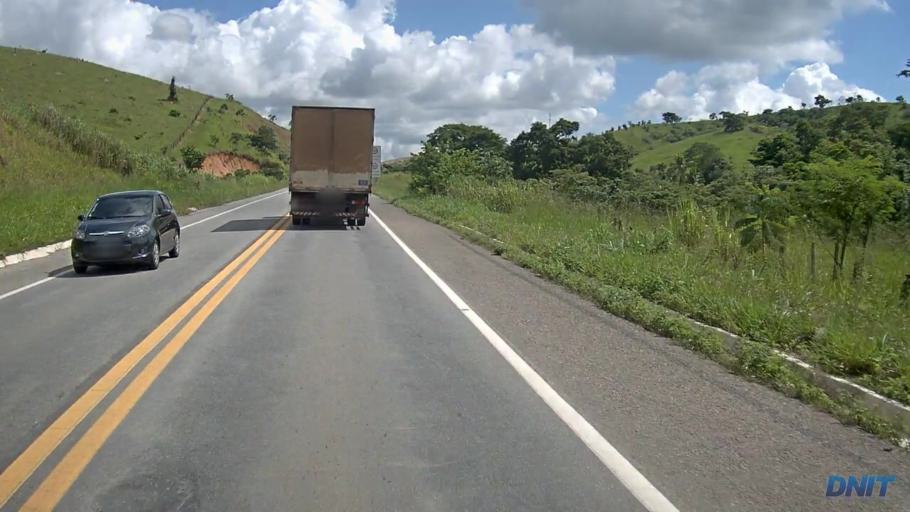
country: BR
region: Minas Gerais
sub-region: Governador Valadares
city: Governador Valadares
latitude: -19.0351
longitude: -42.1484
